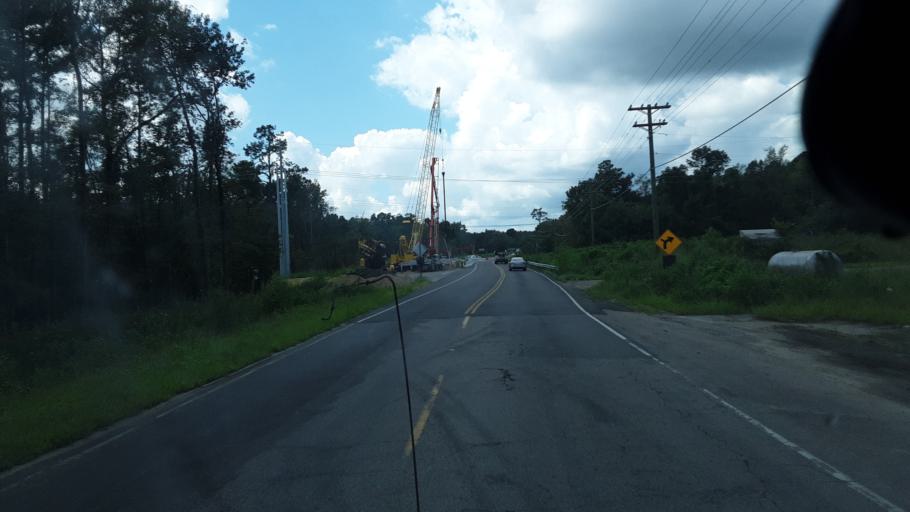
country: US
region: South Carolina
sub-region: Williamsburg County
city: Andrews
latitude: 33.3717
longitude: -79.4487
